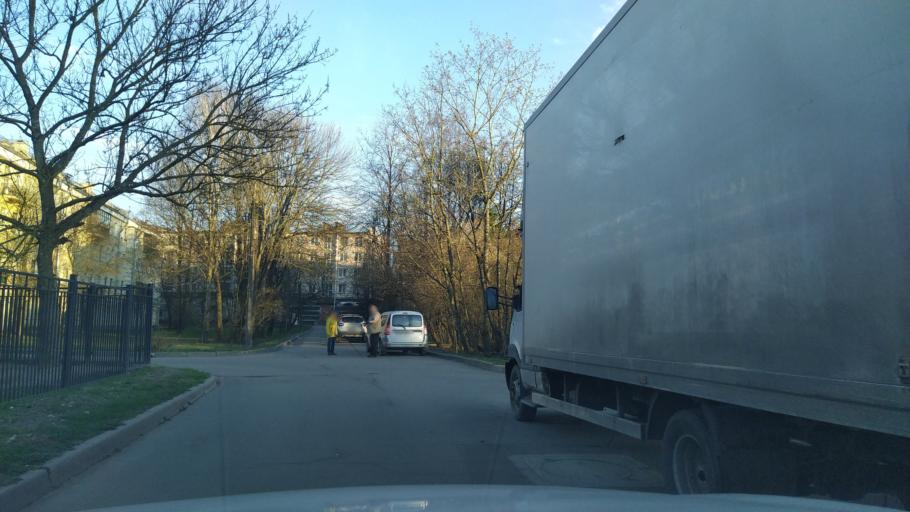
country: RU
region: St.-Petersburg
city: Pushkin
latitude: 59.7053
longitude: 30.3686
